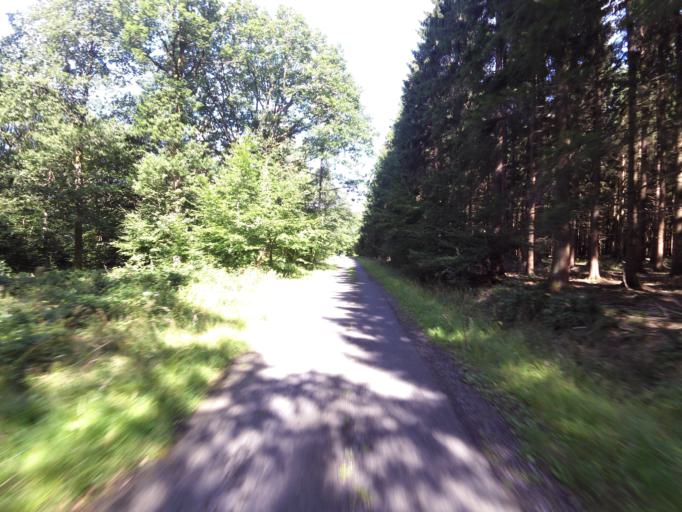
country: BE
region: Wallonia
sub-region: Province du Luxembourg
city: Nassogne
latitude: 50.1245
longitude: 5.3706
